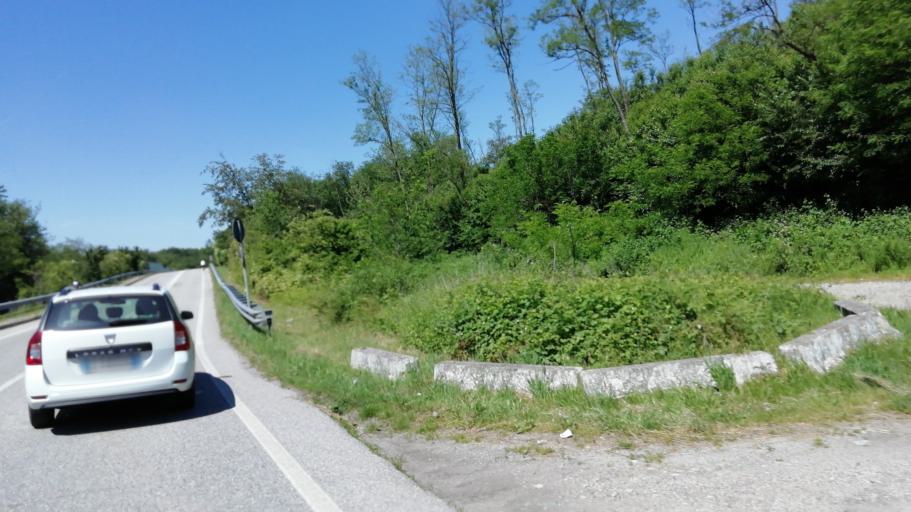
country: IT
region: Lombardy
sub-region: Provincia di Varese
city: Ferno
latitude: 45.6071
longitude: 8.7418
